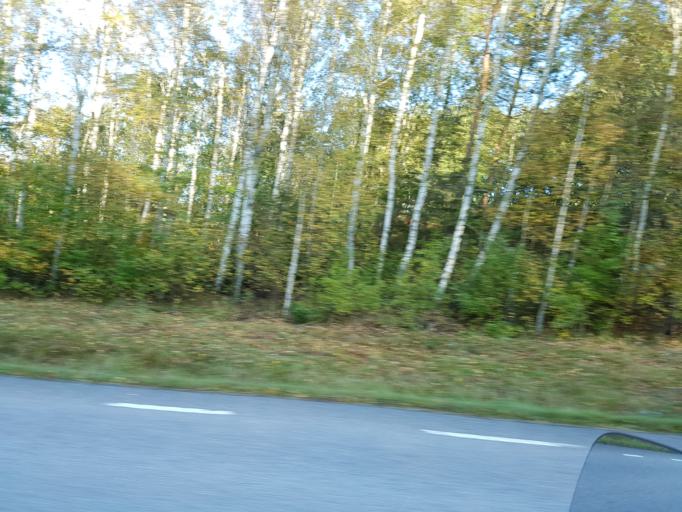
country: SE
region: Vaestra Goetaland
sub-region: Tjorns Kommun
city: Myggenas
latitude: 58.0644
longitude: 11.7413
